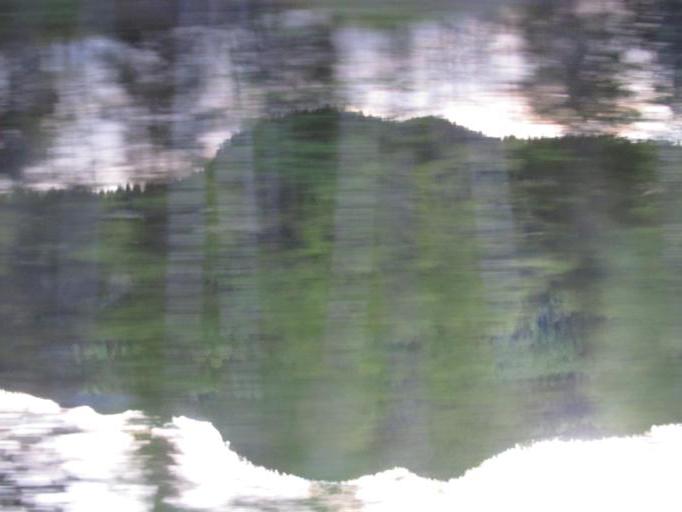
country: NO
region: Oppland
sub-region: Oyer
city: Tretten
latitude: 61.2821
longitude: 10.2865
